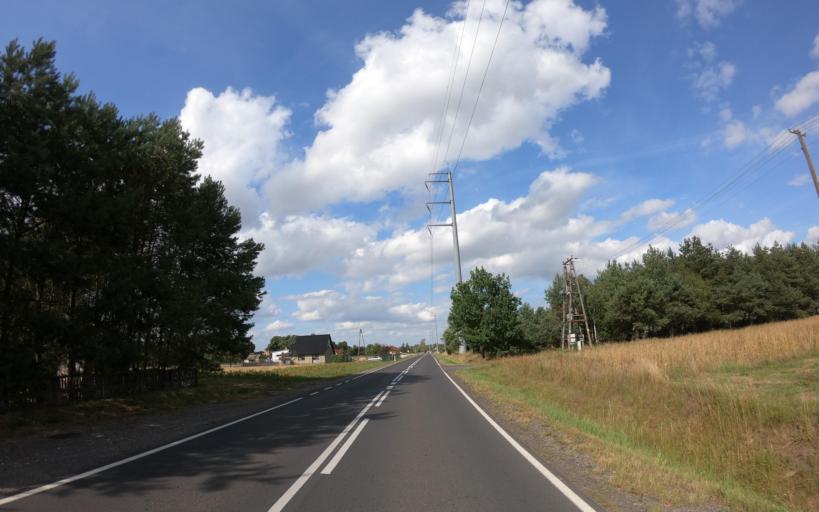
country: PL
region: West Pomeranian Voivodeship
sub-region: Powiat drawski
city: Czaplinek
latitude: 53.5133
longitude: 16.2228
